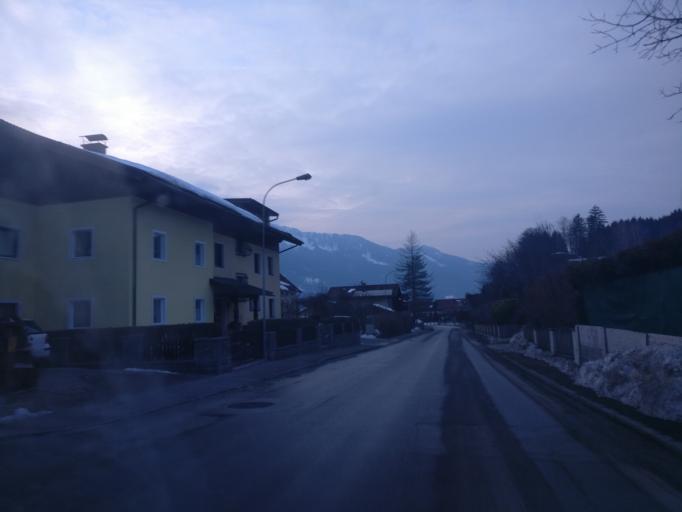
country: AT
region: Salzburg
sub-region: Politischer Bezirk Hallein
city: Golling an der Salzach
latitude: 47.6165
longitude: 13.1739
